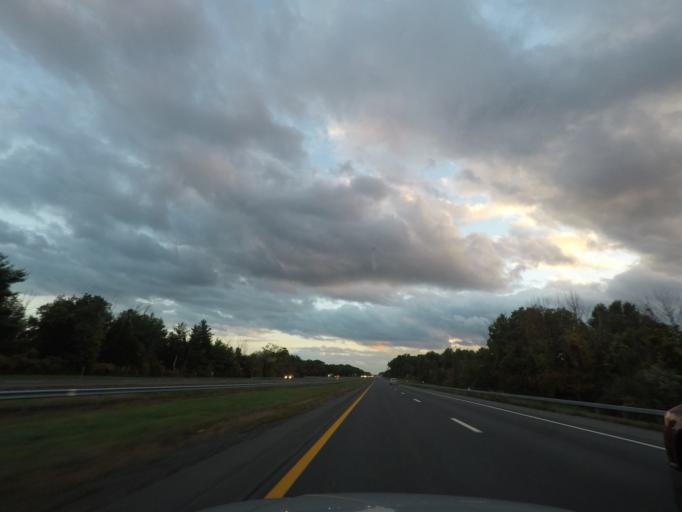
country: US
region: New York
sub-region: Ulster County
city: Saugerties South
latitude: 42.0587
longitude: -73.9825
